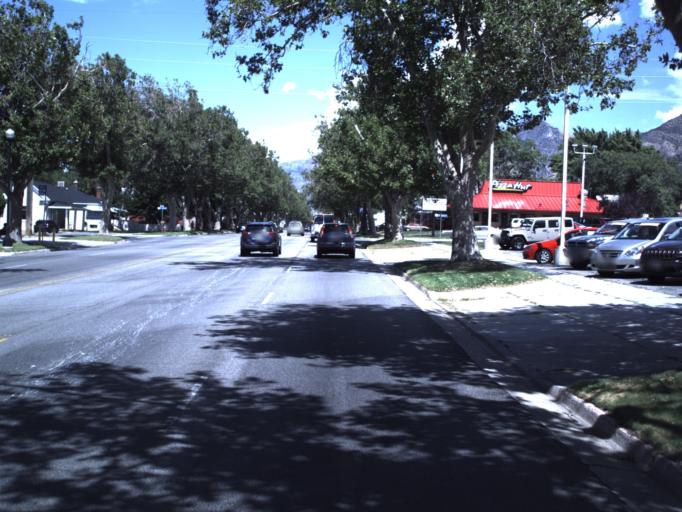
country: US
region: Utah
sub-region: Box Elder County
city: Brigham City
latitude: 41.4977
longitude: -112.0160
